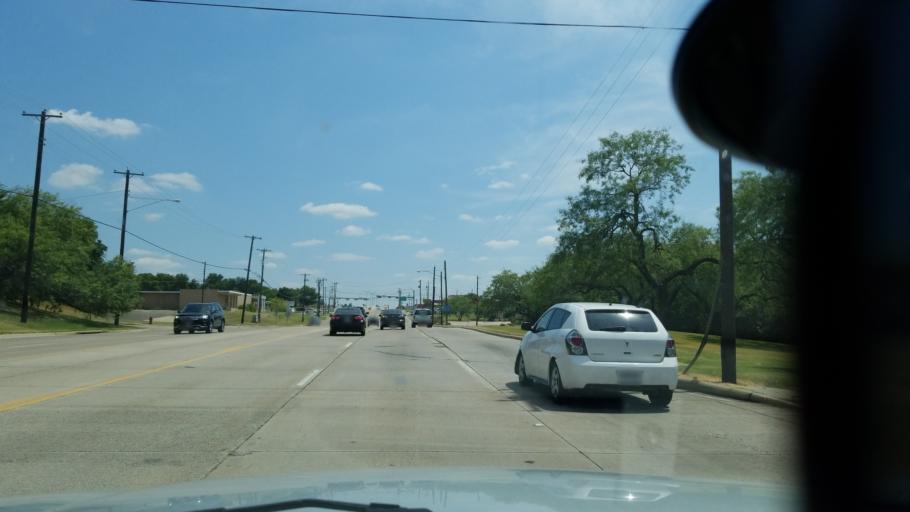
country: US
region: Texas
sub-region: Dallas County
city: Grand Prairie
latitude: 32.7515
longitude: -96.9948
